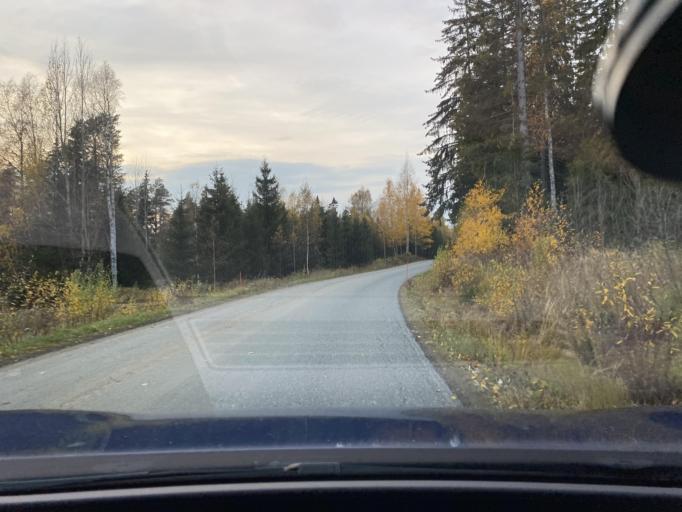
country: FI
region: Varsinais-Suomi
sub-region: Loimaa
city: Alastaro
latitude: 61.0830
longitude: 22.9345
